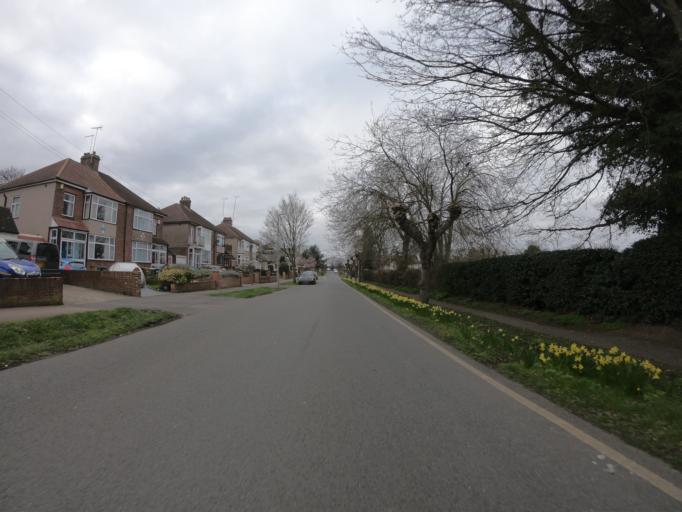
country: GB
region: England
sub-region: Greater London
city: Erith
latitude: 51.4777
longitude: 0.1690
